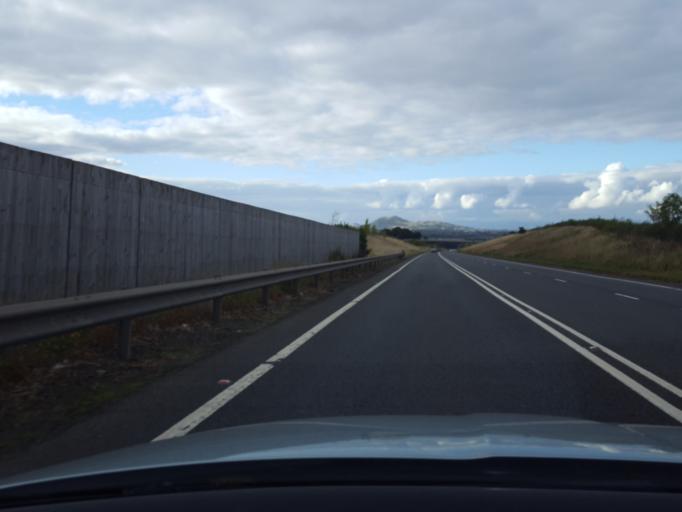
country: GB
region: Scotland
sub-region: Midlothian
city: Dalkeith
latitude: 55.9000
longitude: -3.0204
